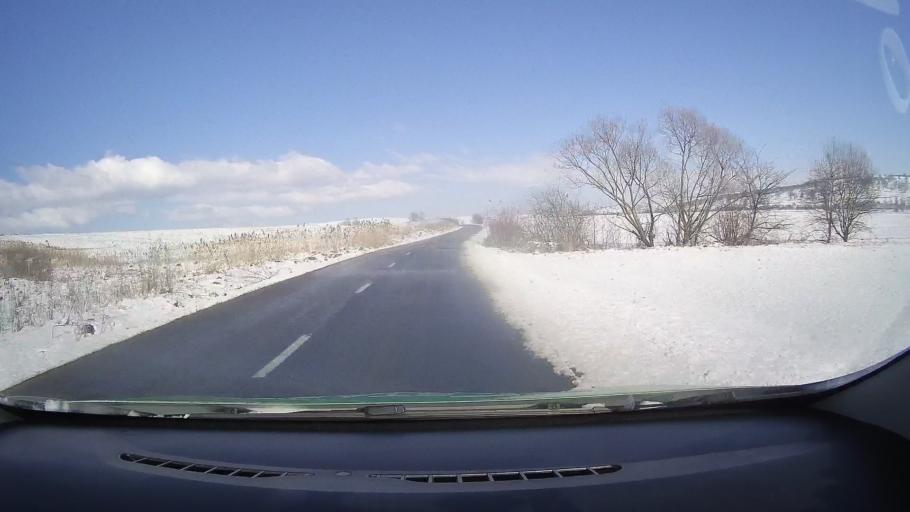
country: RO
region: Sibiu
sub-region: Comuna Rosia
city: Rosia
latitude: 45.8442
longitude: 24.3056
